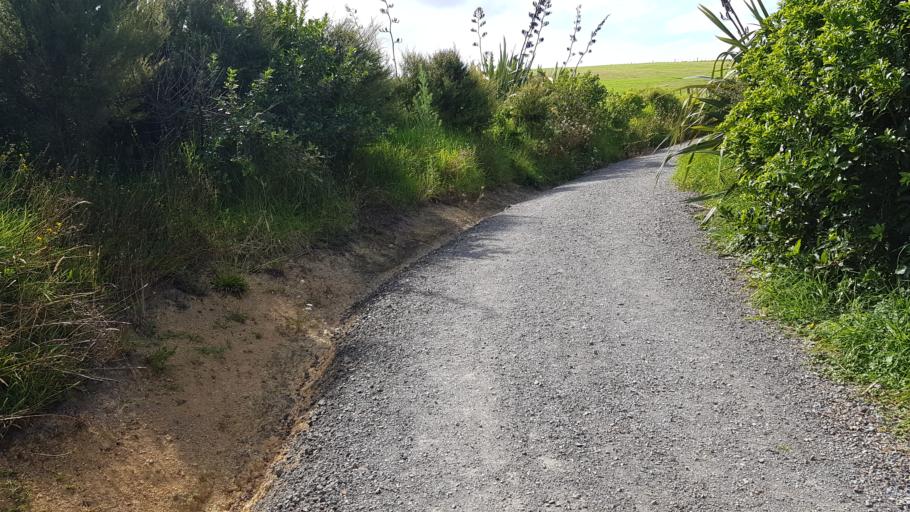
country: NZ
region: Auckland
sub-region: Auckland
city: Rothesay Bay
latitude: -36.6731
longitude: 174.7459
